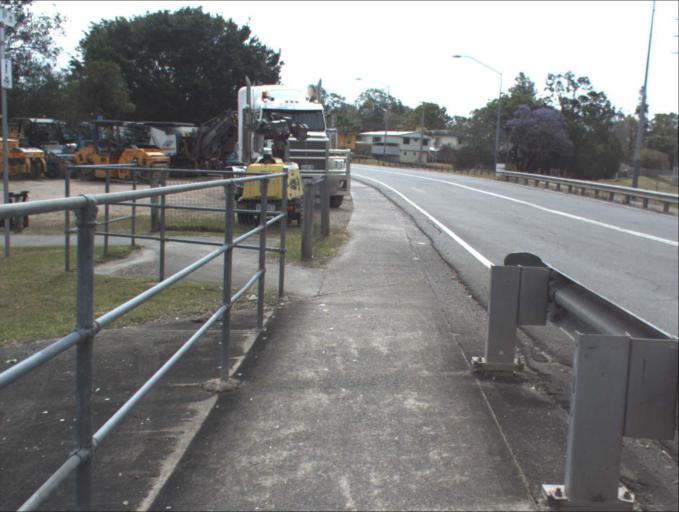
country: AU
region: Queensland
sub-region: Logan
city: Springwood
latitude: -27.6266
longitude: 153.1270
